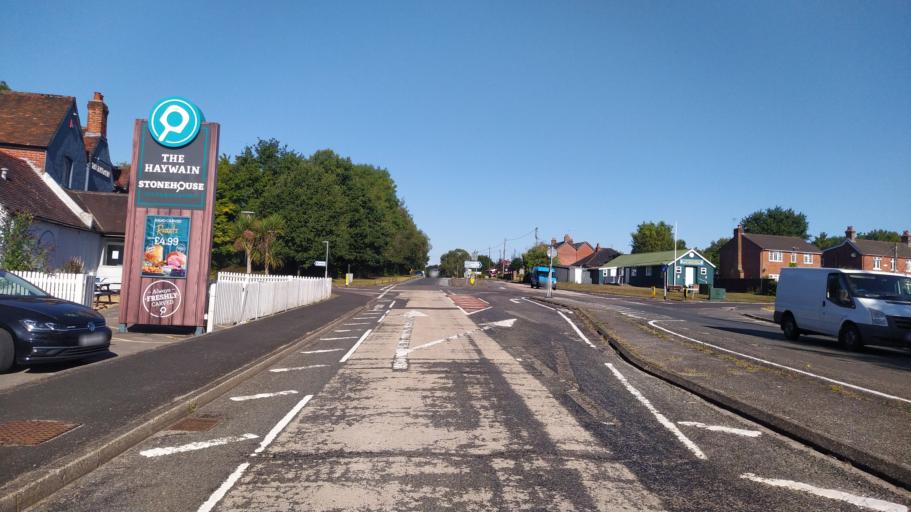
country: GB
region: England
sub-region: Hampshire
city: Cadnam
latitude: 50.9176
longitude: -1.5644
